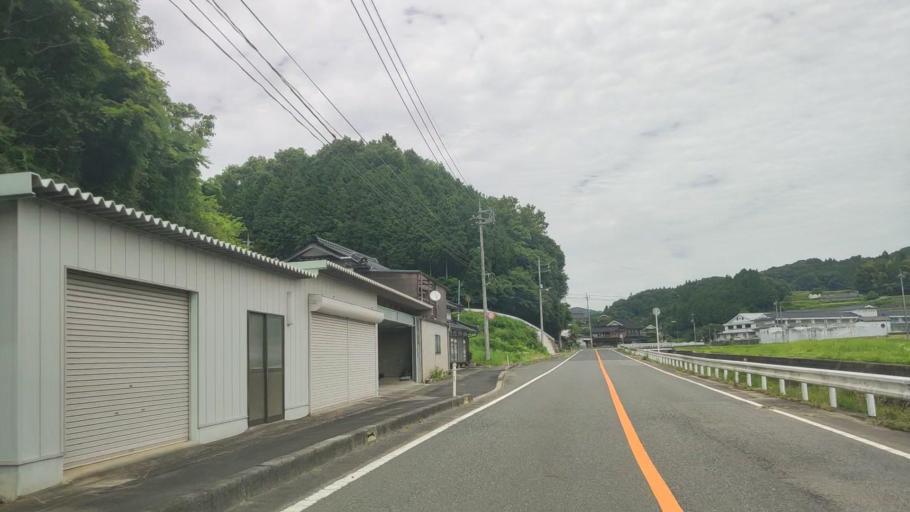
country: JP
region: Okayama
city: Tsuyama
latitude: 35.0742
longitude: 134.2425
